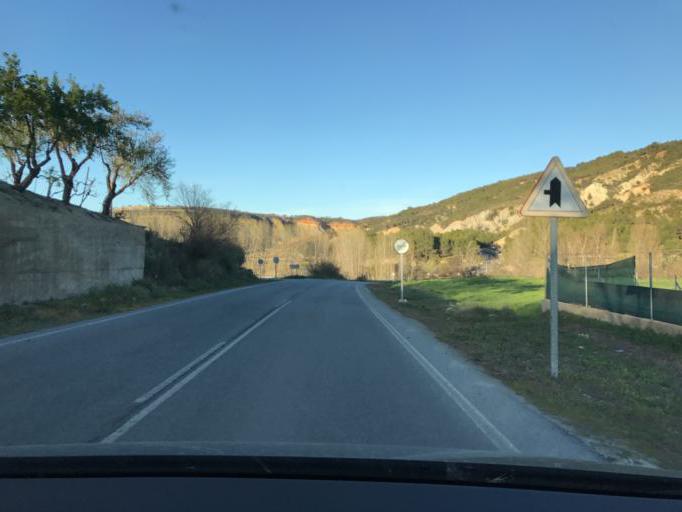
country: ES
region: Andalusia
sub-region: Provincia de Granada
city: Policar
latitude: 37.2834
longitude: -3.2813
